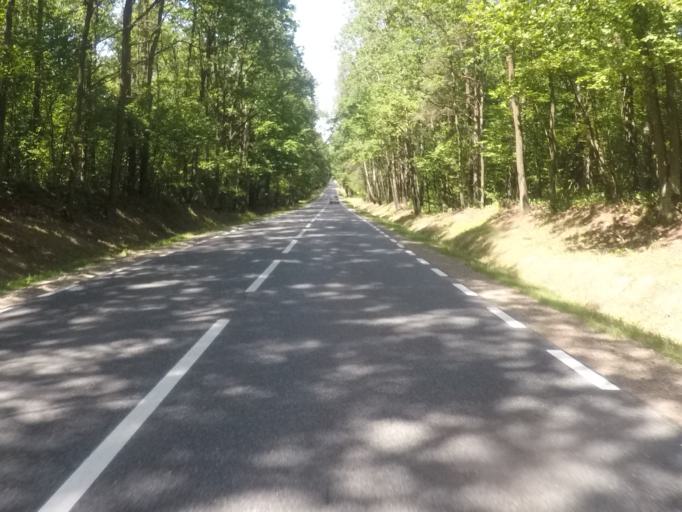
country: PL
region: Masovian Voivodeship
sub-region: Powiat losicki
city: Sarnaki
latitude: 52.3421
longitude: 22.8756
